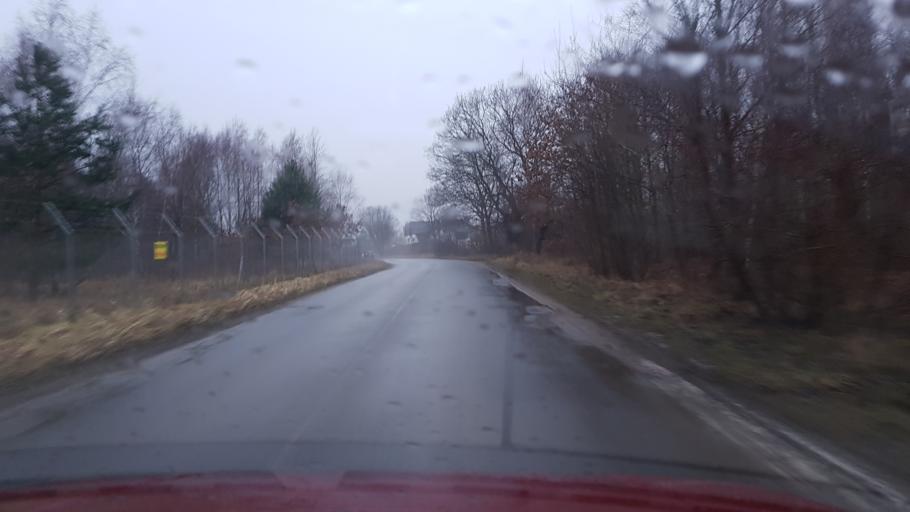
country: PL
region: West Pomeranian Voivodeship
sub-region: Koszalin
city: Koszalin
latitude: 54.1785
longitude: 16.2252
